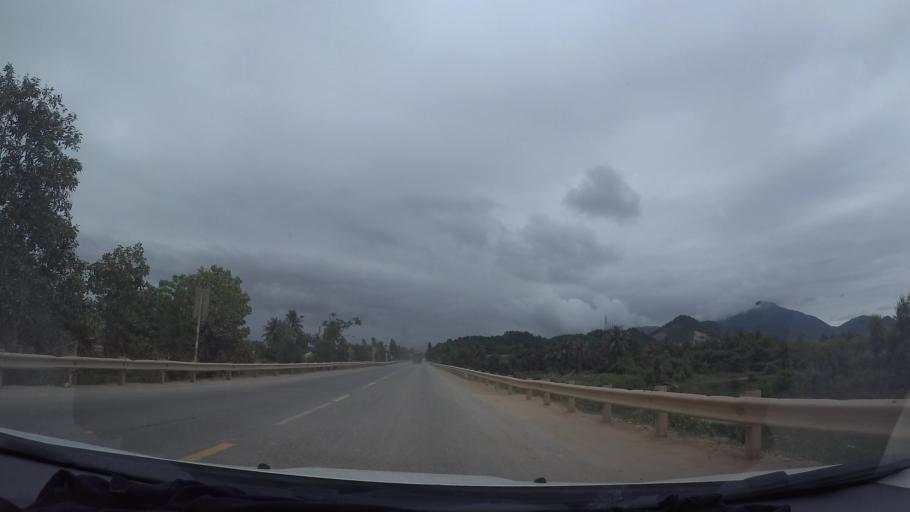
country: VN
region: Da Nang
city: Lien Chieu
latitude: 16.1059
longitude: 108.1017
